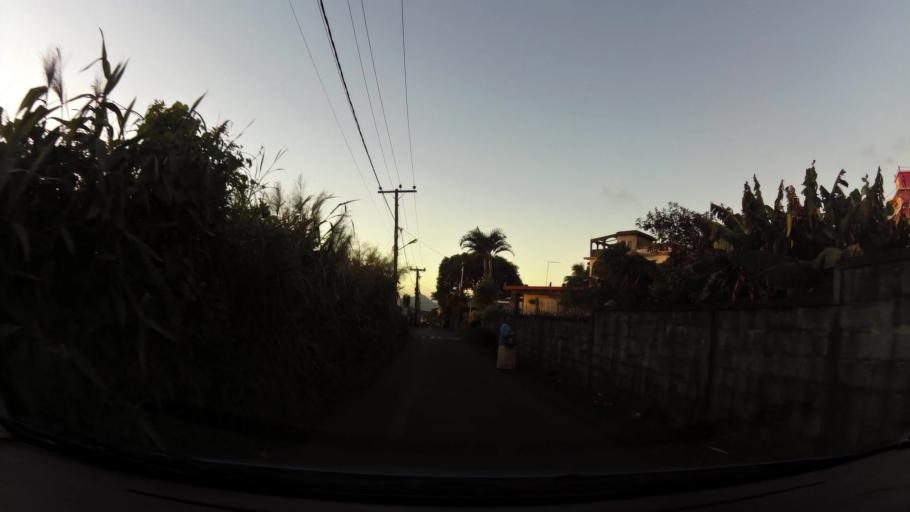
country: MU
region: Plaines Wilhems
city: Curepipe
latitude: -20.3004
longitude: 57.5233
